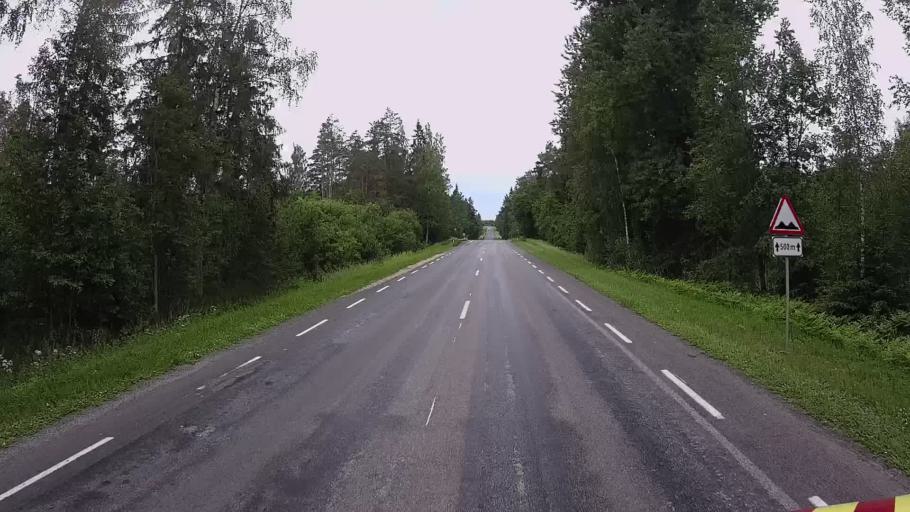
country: EE
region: Viljandimaa
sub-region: Karksi vald
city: Karksi-Nuia
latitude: 58.1886
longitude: 25.6021
